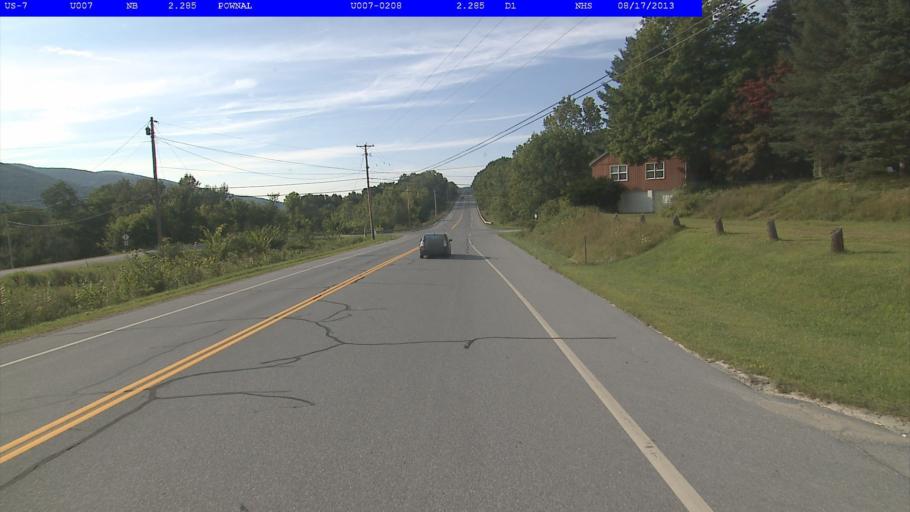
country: US
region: Massachusetts
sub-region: Berkshire County
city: Williamstown
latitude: 42.7691
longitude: -73.2352
